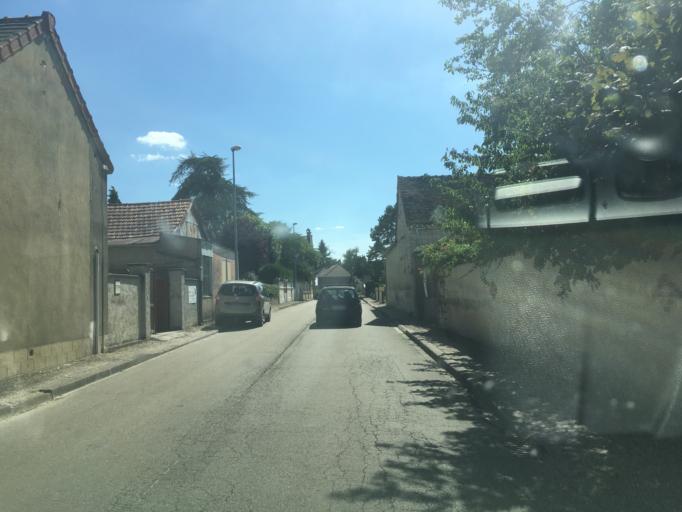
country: FR
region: Bourgogne
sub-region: Departement de l'Yonne
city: Fleury-la-Vallee
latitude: 47.8648
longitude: 3.4472
